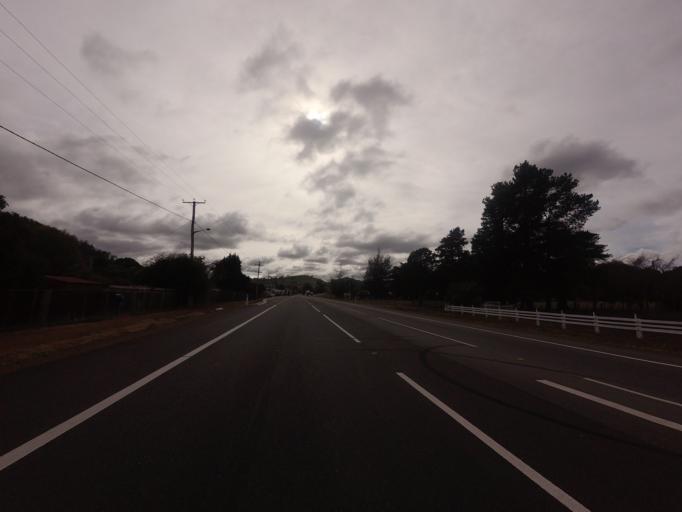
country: AU
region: Tasmania
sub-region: Brighton
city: Bridgewater
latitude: -42.6046
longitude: 147.2205
